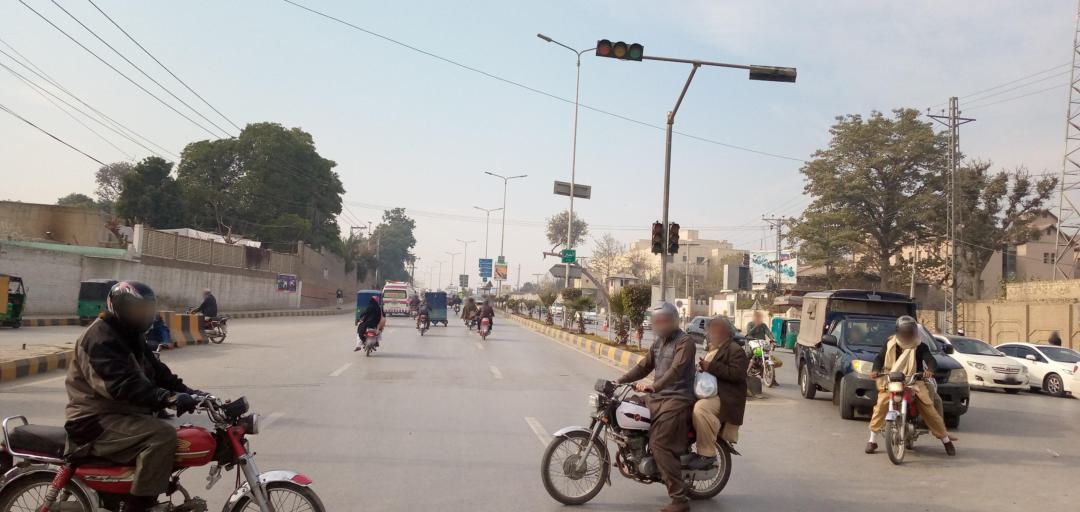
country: PK
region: Khyber Pakhtunkhwa
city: Peshawar
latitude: 34.0146
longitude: 71.5560
